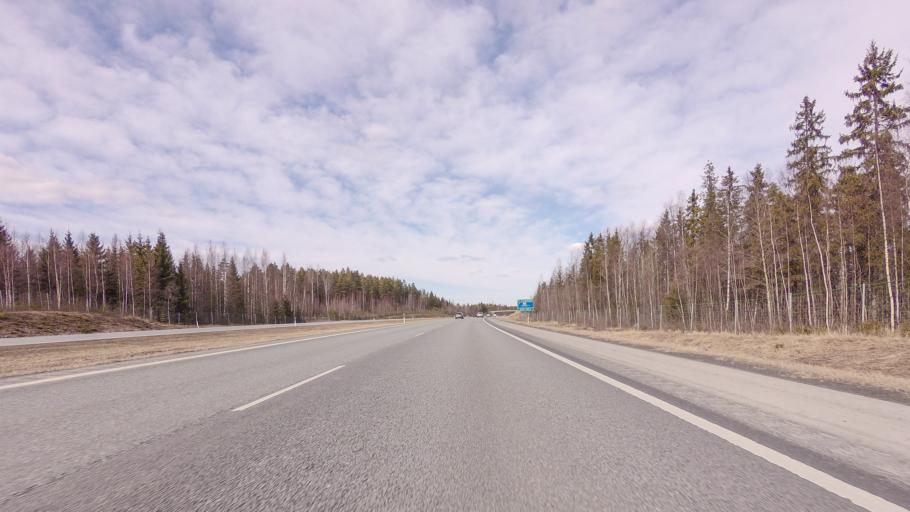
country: FI
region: Pirkanmaa
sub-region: Tampere
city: Lempaeaelae
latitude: 61.2760
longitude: 23.8121
